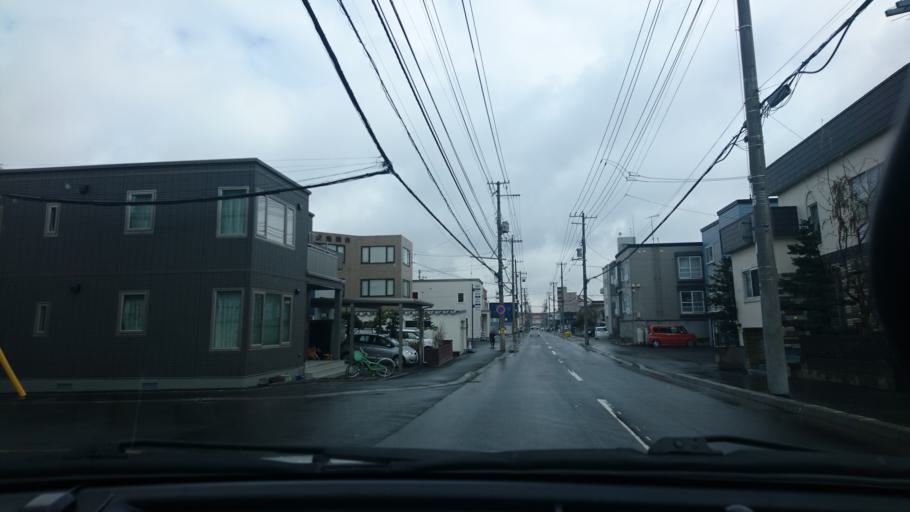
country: JP
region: Hokkaido
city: Sapporo
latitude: 43.0973
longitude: 141.2713
